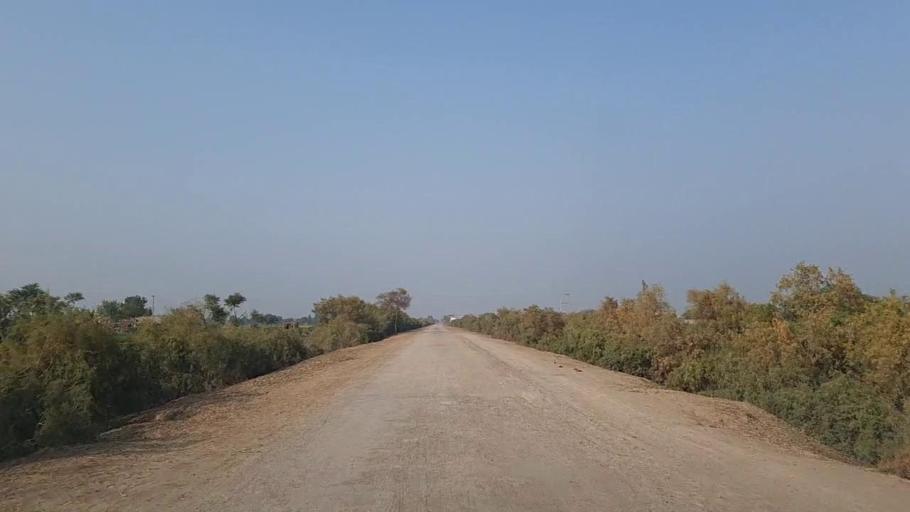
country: PK
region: Sindh
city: Nawabshah
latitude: 26.3354
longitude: 68.4891
